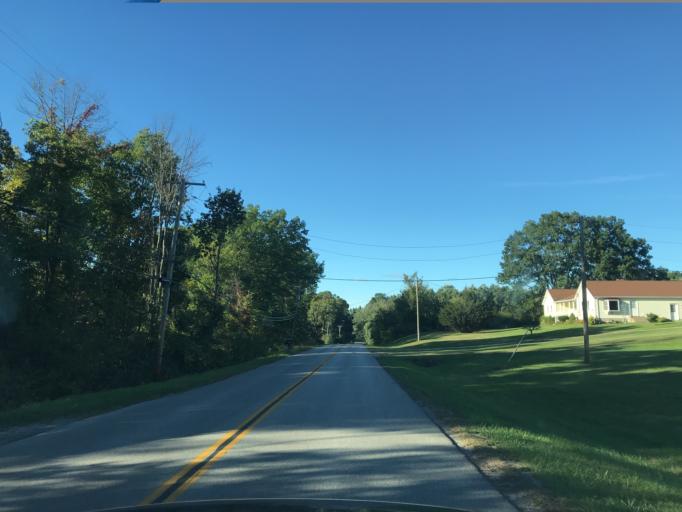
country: US
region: Ohio
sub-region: Ashtabula County
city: Edgewood
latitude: 41.8469
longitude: -80.7560
